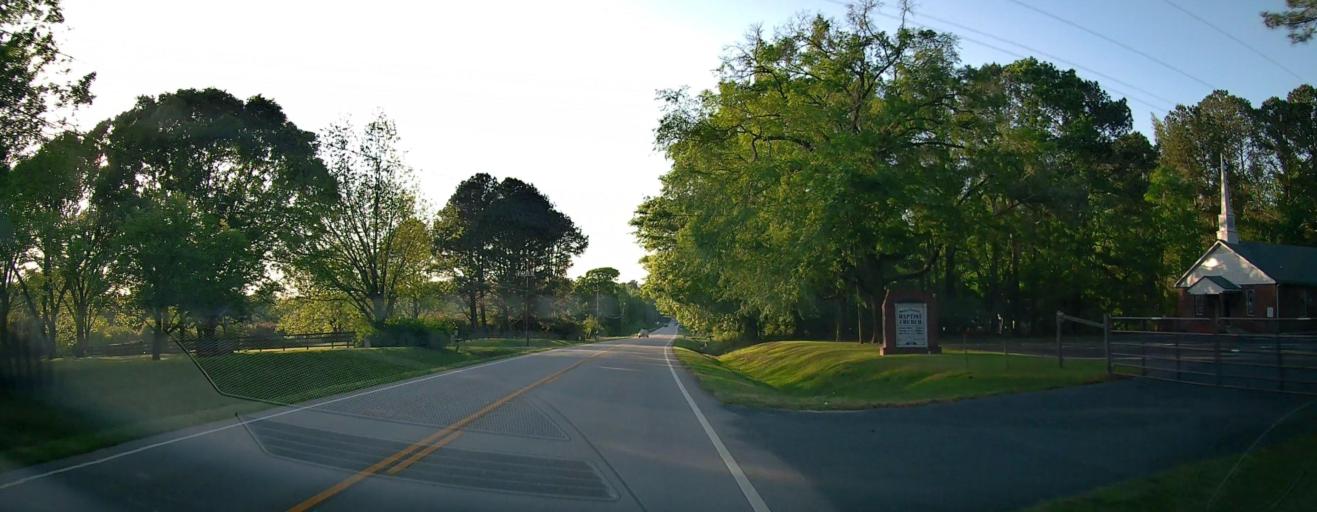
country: US
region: Georgia
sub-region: Newton County
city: Covington
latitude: 33.5804
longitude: -83.7791
